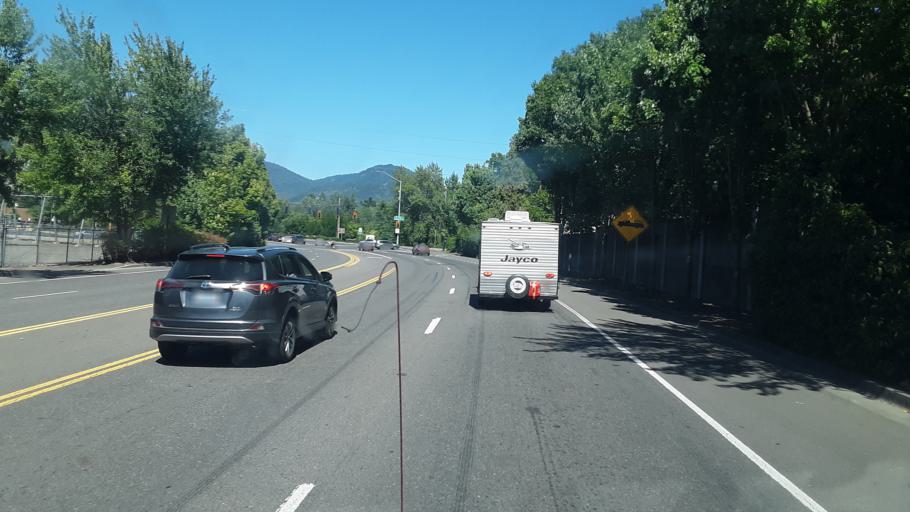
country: US
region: Oregon
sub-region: Josephine County
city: Fruitdale
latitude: 42.4266
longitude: -123.3215
